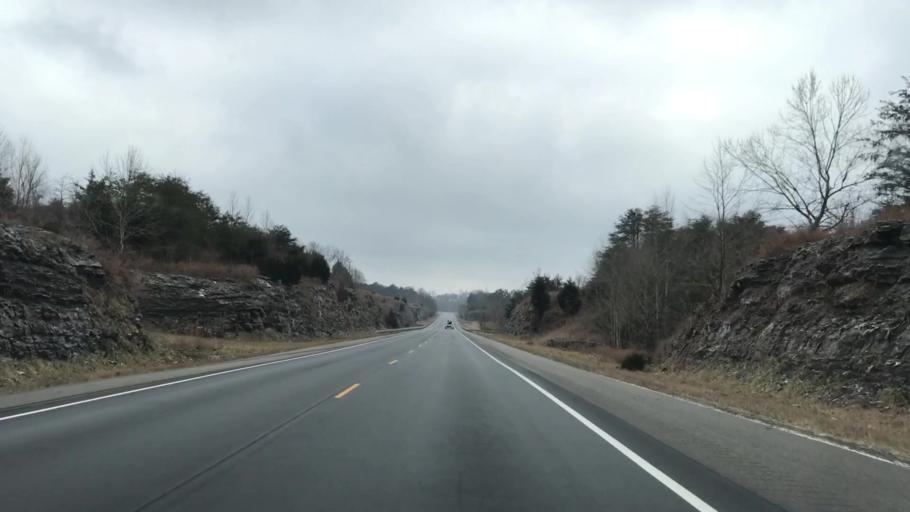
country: US
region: Kentucky
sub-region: Metcalfe County
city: Edmonton
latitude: 36.9503
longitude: -85.4456
